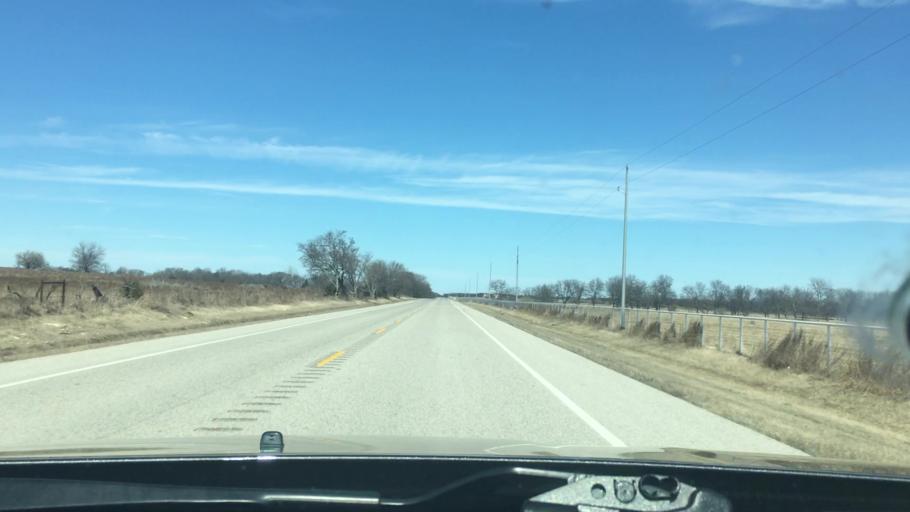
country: US
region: Oklahoma
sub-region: Murray County
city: Sulphur
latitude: 34.3656
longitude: -96.9508
